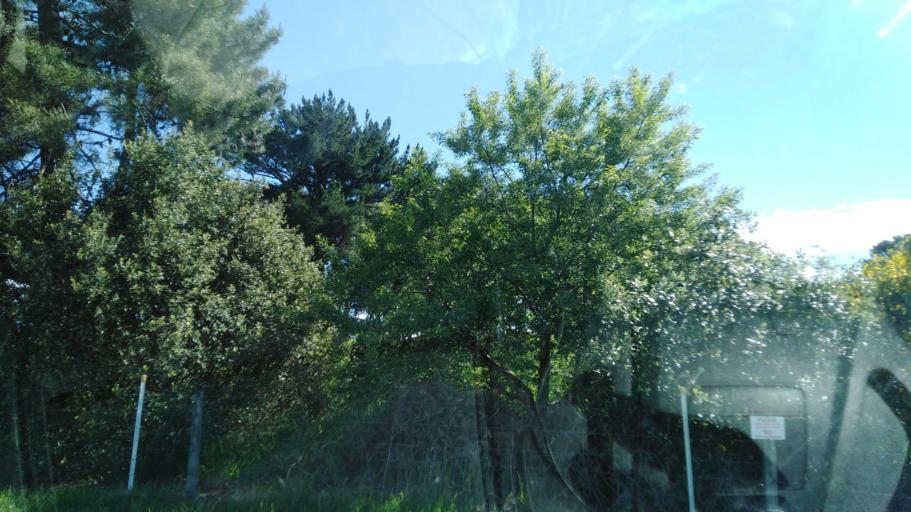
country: NZ
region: Waikato
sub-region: Taupo District
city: Taupo
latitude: -38.7396
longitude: 176.0801
